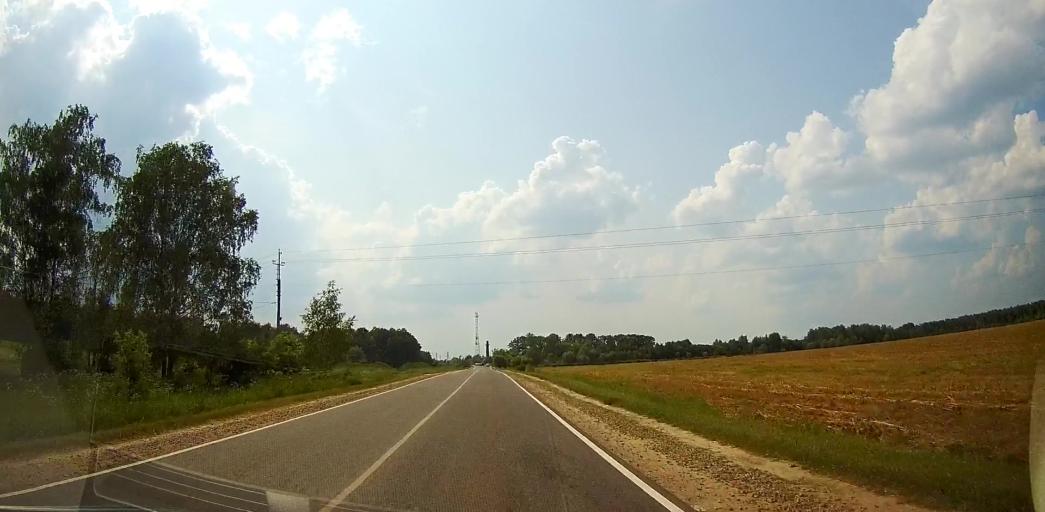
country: RU
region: Moskovskaya
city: Zhilevo
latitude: 55.0535
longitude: 38.0018
